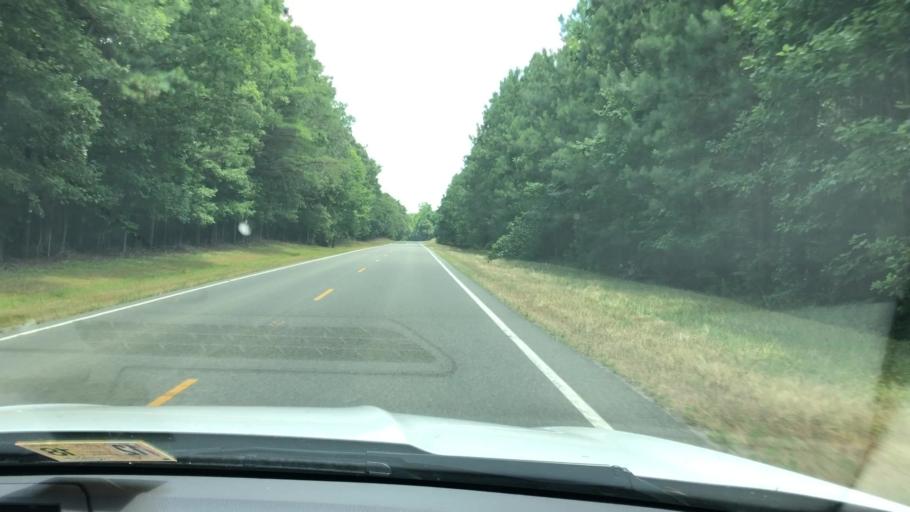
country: US
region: Virginia
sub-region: Lancaster County
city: Lancaster
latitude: 37.8050
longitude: -76.5359
